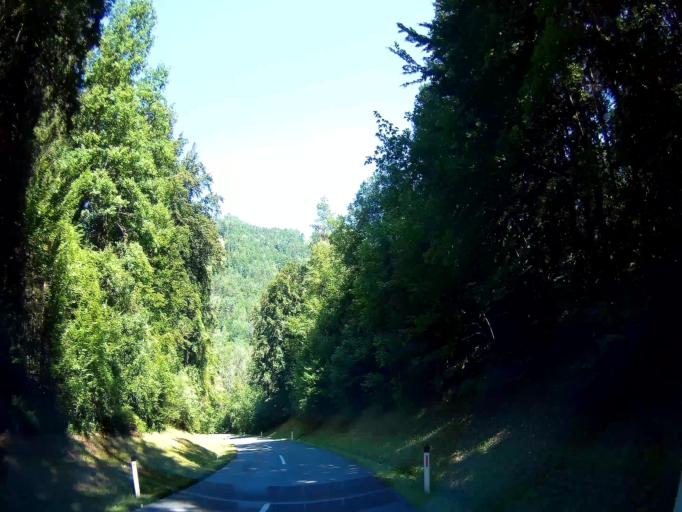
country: AT
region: Carinthia
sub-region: Politischer Bezirk Klagenfurt Land
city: Grafenstein
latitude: 46.5974
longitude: 14.4353
